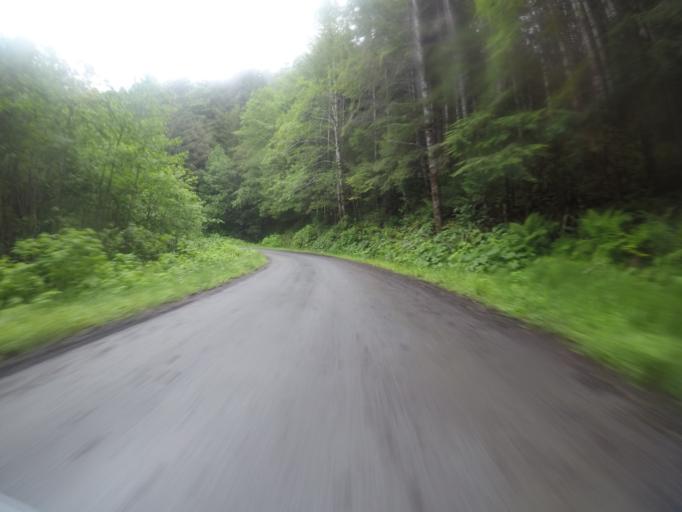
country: US
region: California
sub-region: Humboldt County
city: Westhaven-Moonstone
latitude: 41.2295
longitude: -123.9904
